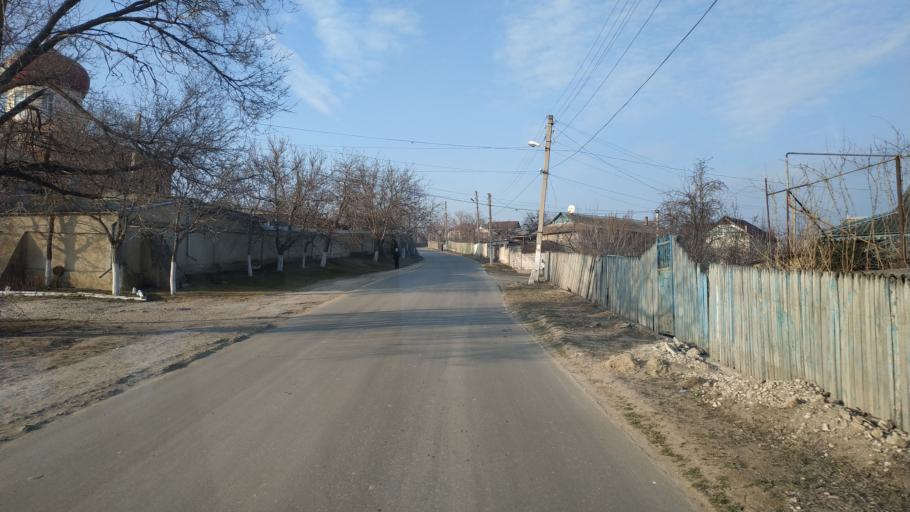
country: MD
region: Hincesti
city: Dancu
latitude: 46.7657
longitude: 28.3597
